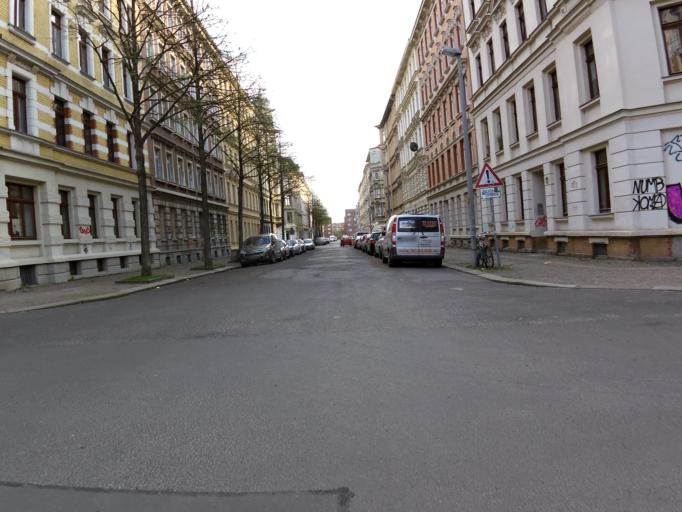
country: DE
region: Saxony
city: Leipzig
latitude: 51.3460
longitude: 12.4111
